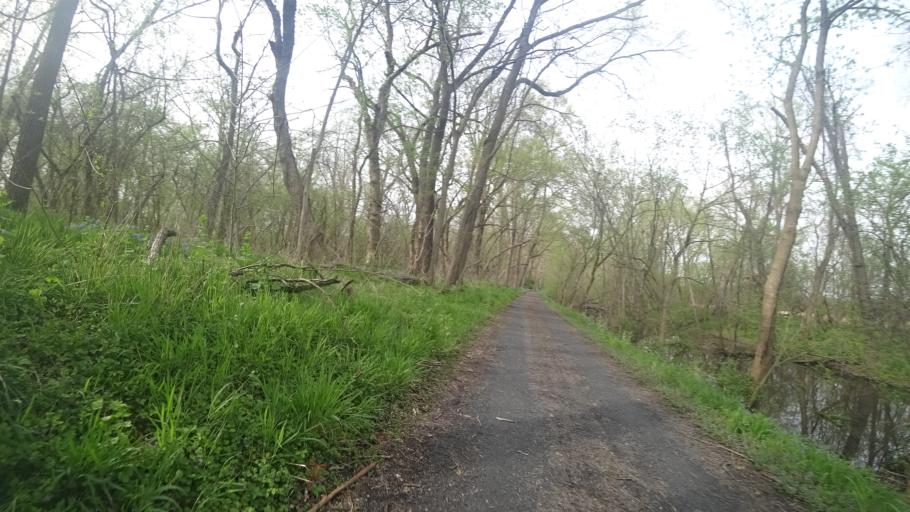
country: US
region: Virginia
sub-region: Loudoun County
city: Leesburg
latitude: 39.1655
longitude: -77.5151
